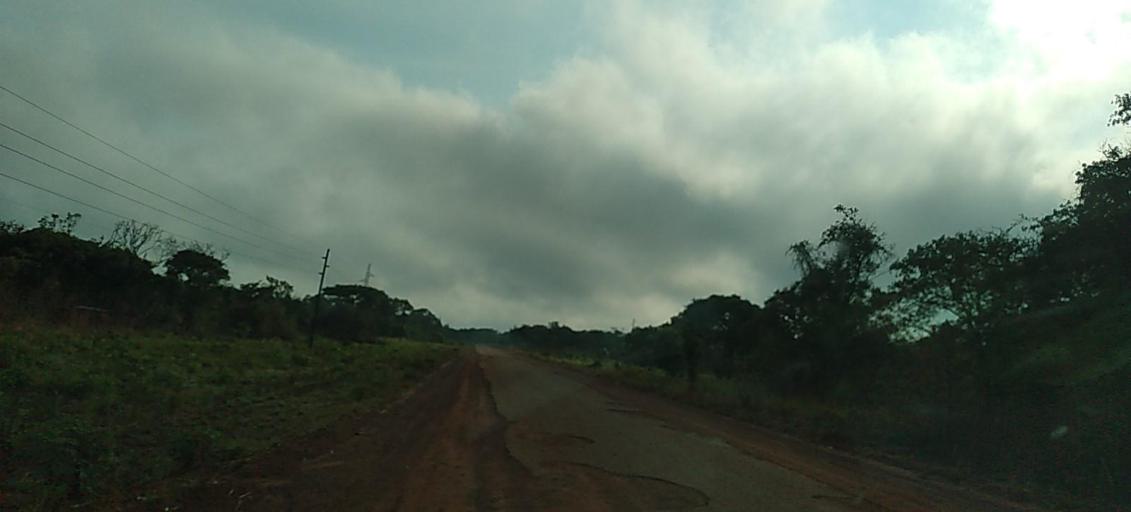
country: ZM
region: North-Western
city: Mwinilunga
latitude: -11.7273
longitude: 24.4925
